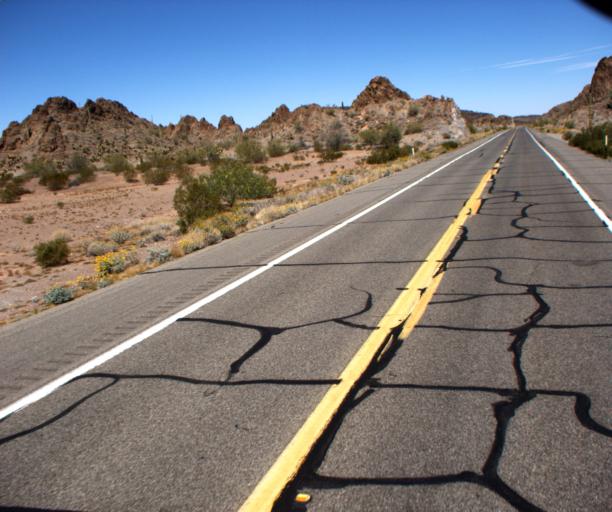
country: US
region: Arizona
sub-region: Pima County
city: Ajo
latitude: 32.5432
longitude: -112.8800
